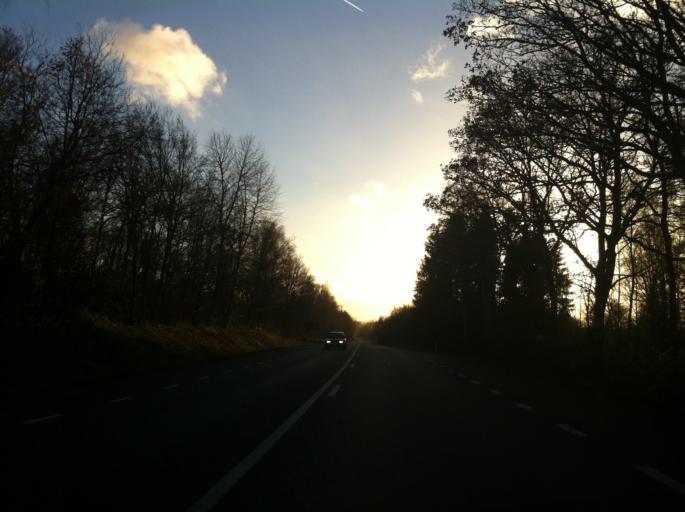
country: SE
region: Skane
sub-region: Hassleholms Kommun
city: Hassleholm
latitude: 56.1346
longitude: 13.8004
